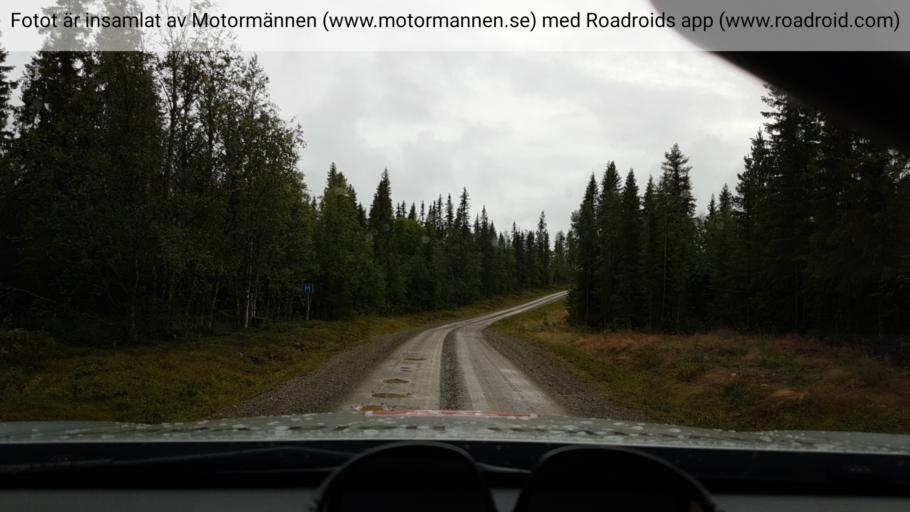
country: SE
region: Vaesterbotten
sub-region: Storumans Kommun
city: Storuman
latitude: 64.8480
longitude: 17.4124
